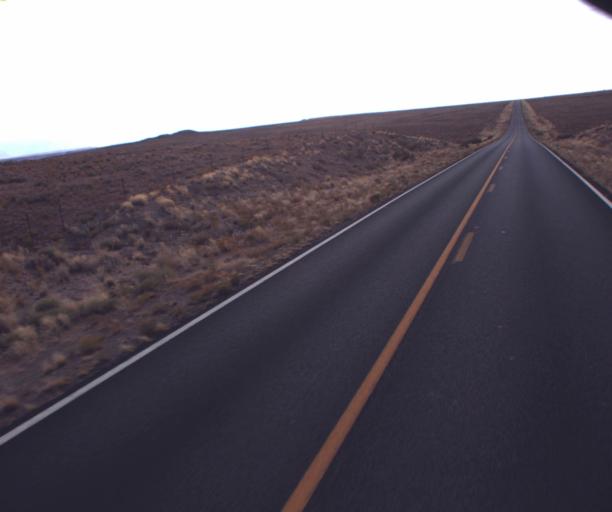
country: US
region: Arizona
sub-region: Apache County
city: Many Farms
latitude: 36.5820
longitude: -109.5558
